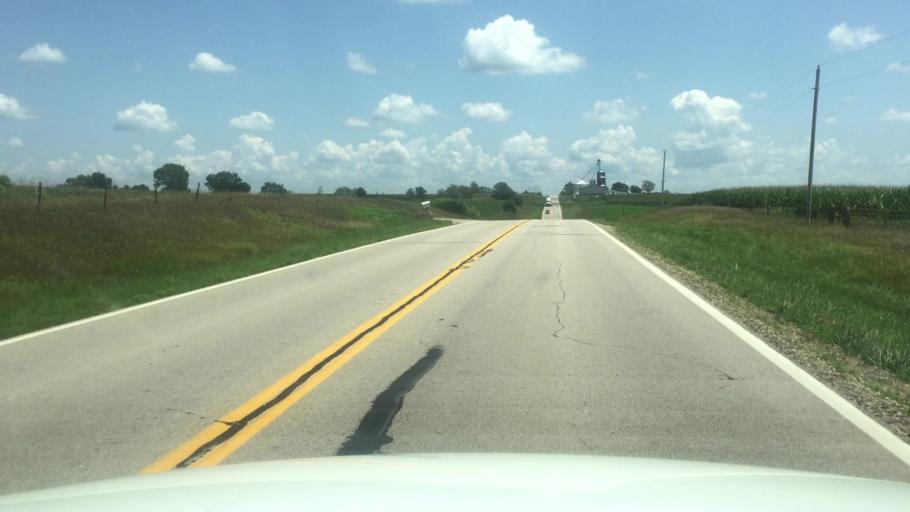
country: US
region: Kansas
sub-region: Brown County
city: Horton
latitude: 39.6673
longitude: -95.6144
